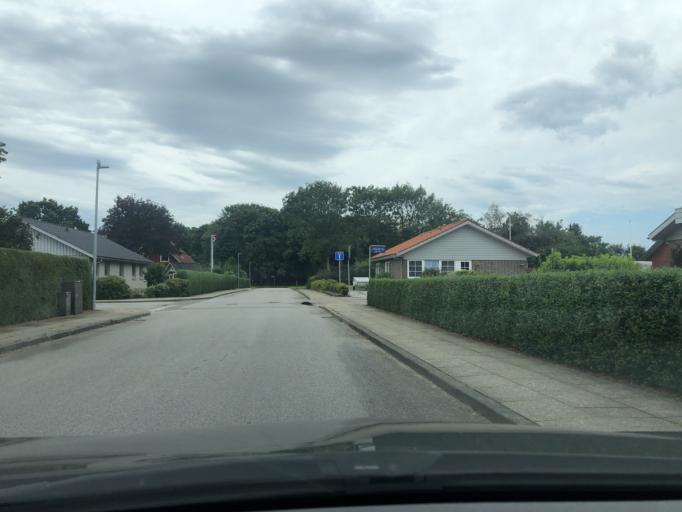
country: DK
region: South Denmark
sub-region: Varde Kommune
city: Olgod
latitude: 55.8064
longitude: 8.6106
